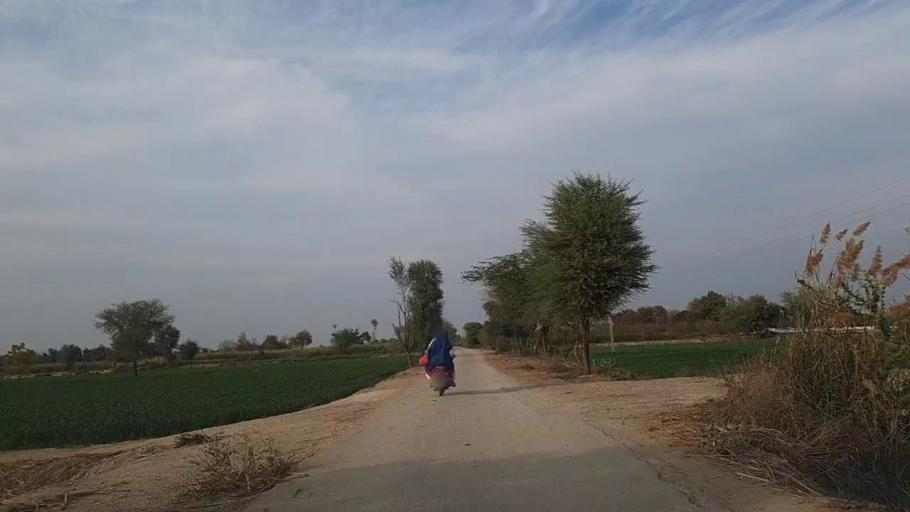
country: PK
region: Sindh
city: Daur
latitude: 26.5222
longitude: 68.4072
